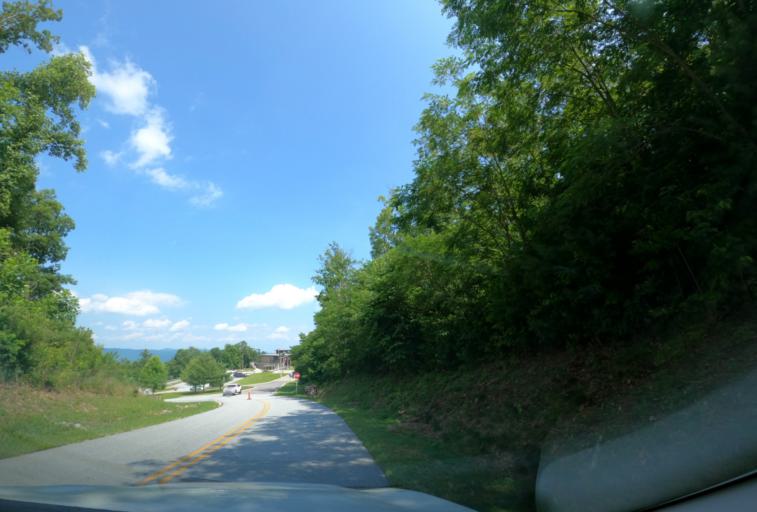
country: US
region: North Carolina
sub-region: Transylvania County
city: Brevard
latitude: 35.0972
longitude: -82.9523
